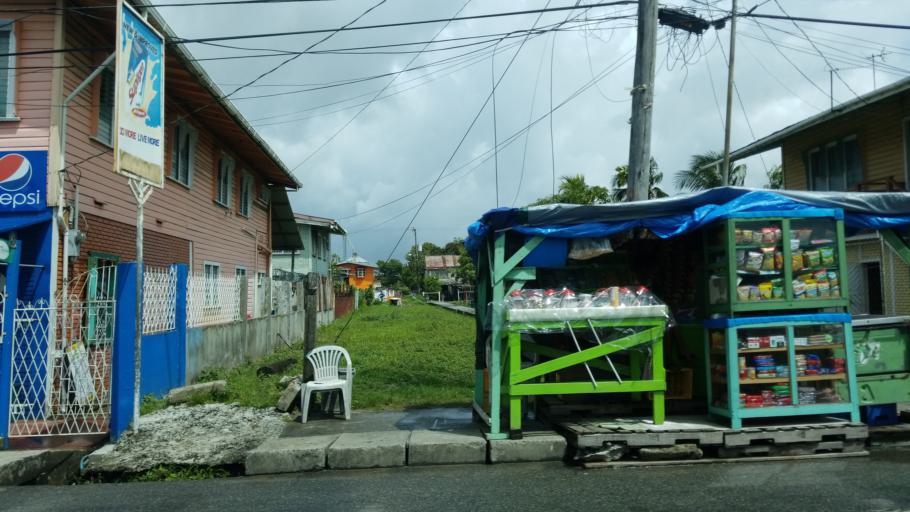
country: GY
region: Demerara-Mahaica
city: Georgetown
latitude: 6.7776
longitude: -58.1714
